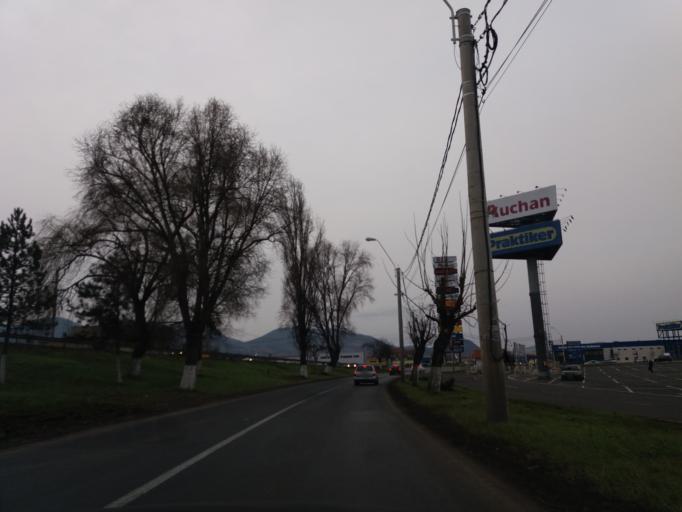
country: RO
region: Hunedoara
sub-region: Municipiul Deva
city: Deva
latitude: 45.8616
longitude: 22.9270
